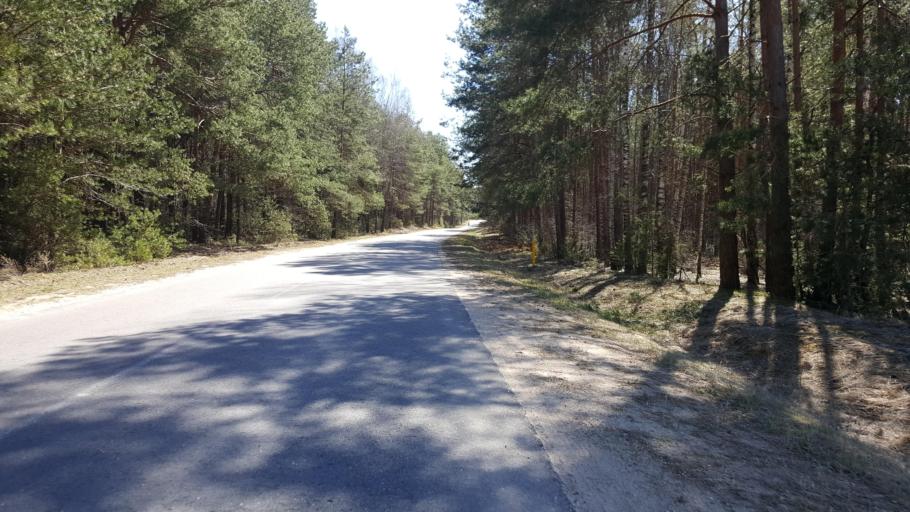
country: BY
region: Brest
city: Kamyanyets
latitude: 52.3611
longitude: 23.8154
